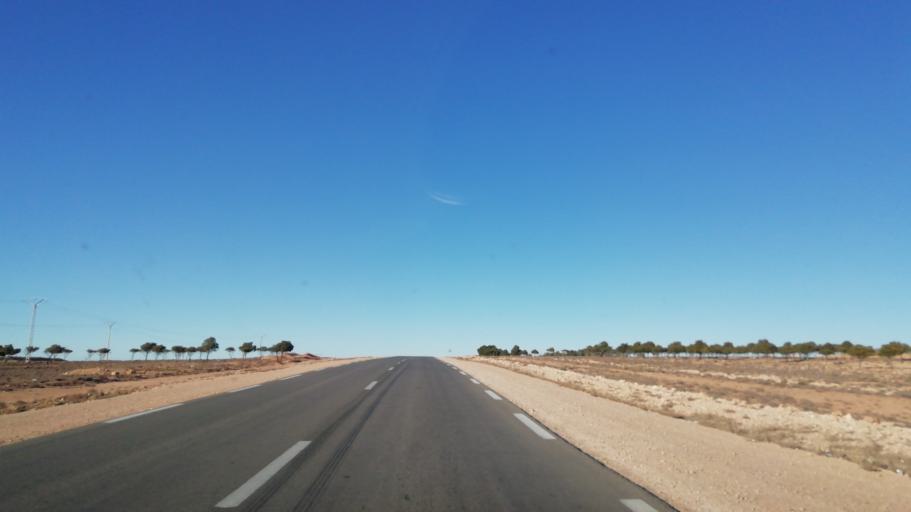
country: DZ
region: Tlemcen
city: Sebdou
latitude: 34.2569
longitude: -1.2577
